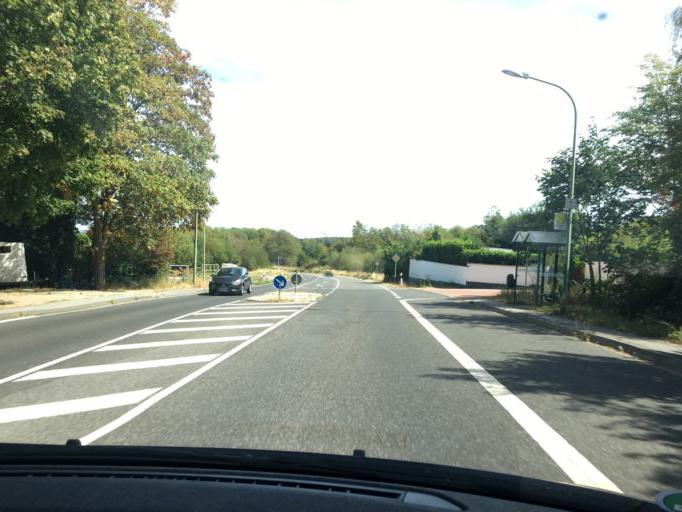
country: DE
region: North Rhine-Westphalia
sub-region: Regierungsbezirk Koln
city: Hurtgenwald
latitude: 50.7441
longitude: 6.4136
